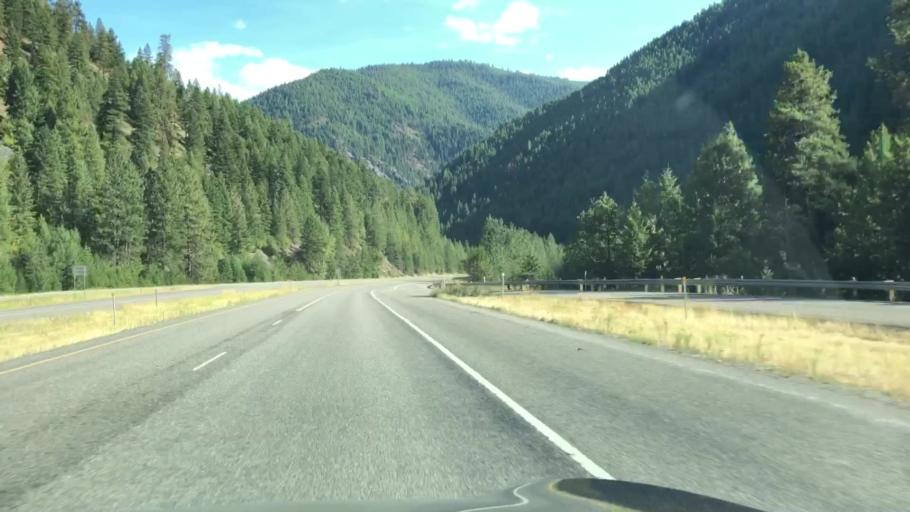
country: US
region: Montana
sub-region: Sanders County
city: Thompson Falls
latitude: 47.3211
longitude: -115.2466
